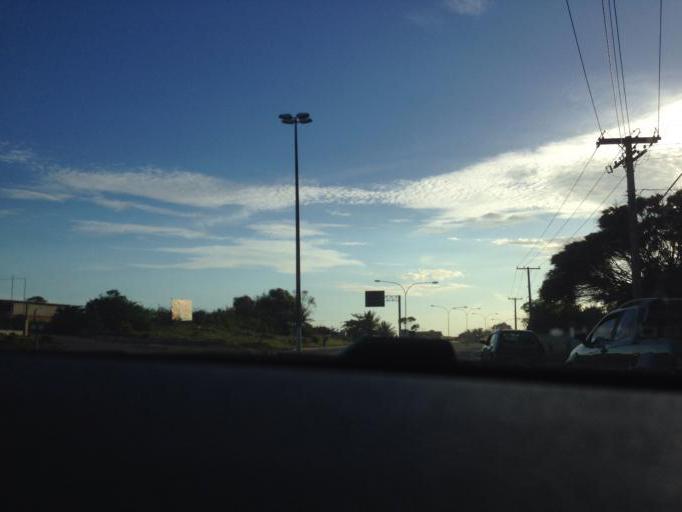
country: BR
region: Espirito Santo
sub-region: Viana
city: Viana
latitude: -20.5160
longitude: -40.3644
